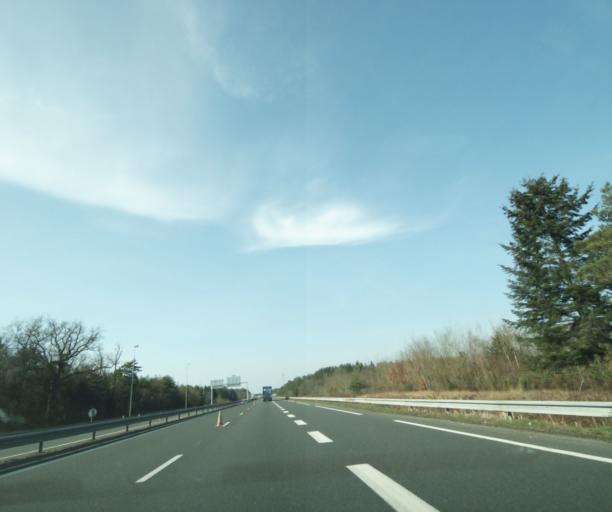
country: FR
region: Centre
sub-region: Departement du Loir-et-Cher
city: Lamotte-Beuvron
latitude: 47.5825
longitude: 1.9946
